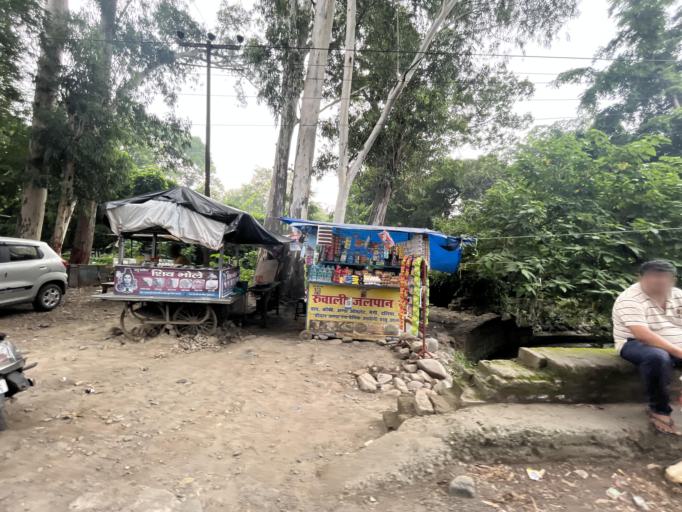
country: IN
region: Uttarakhand
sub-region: Naini Tal
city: Haldwani
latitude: 29.2033
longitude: 79.5166
